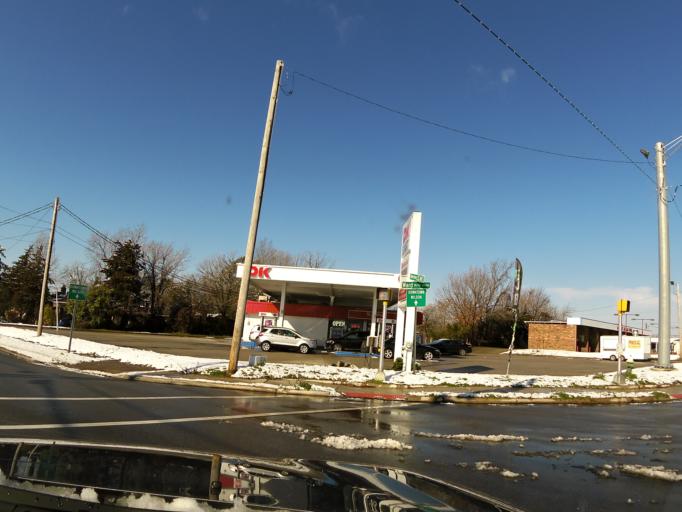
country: US
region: North Carolina
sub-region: Wilson County
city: Wilson
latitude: 35.7294
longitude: -77.8988
